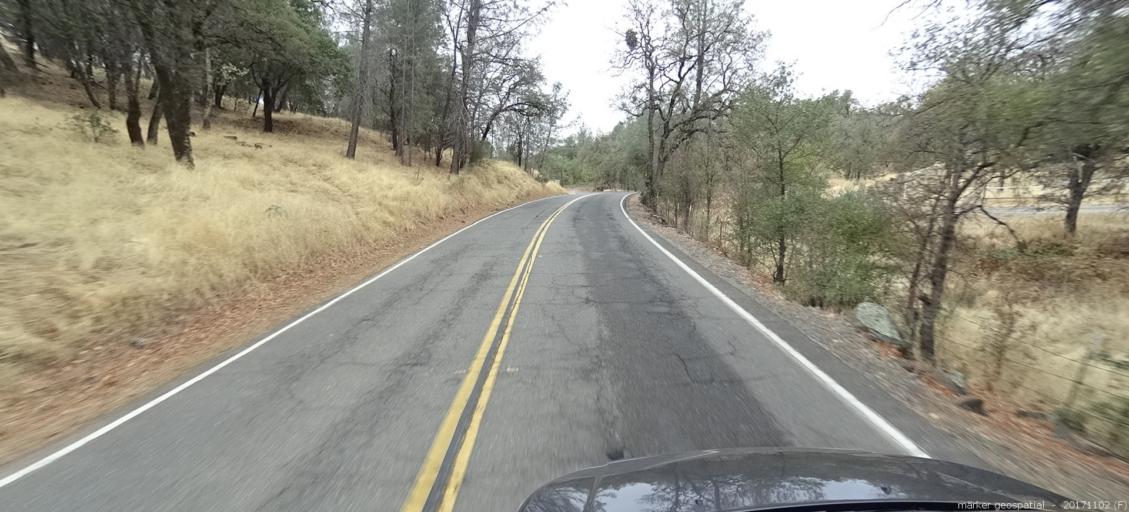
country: US
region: California
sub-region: Shasta County
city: Bella Vista
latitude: 40.7174
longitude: -122.2416
